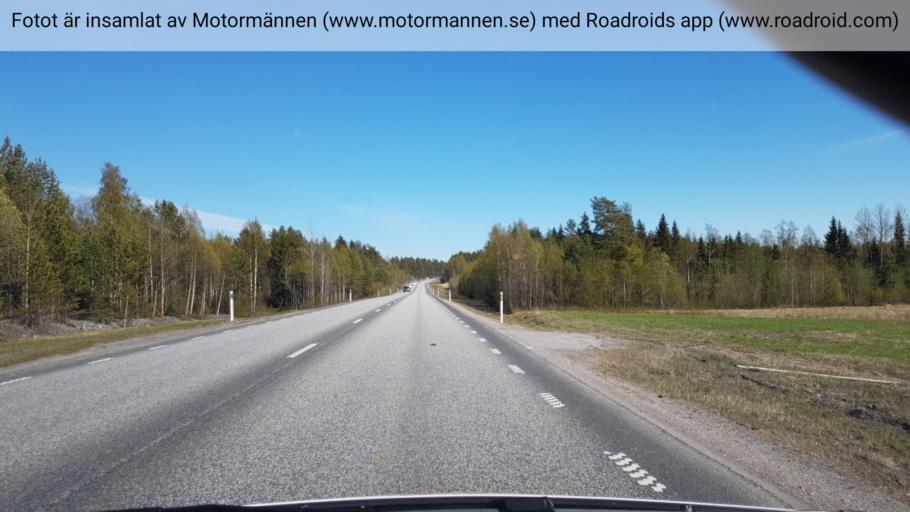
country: SE
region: Vaesterbotten
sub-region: Umea Kommun
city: Roback
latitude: 63.8473
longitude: 20.1405
